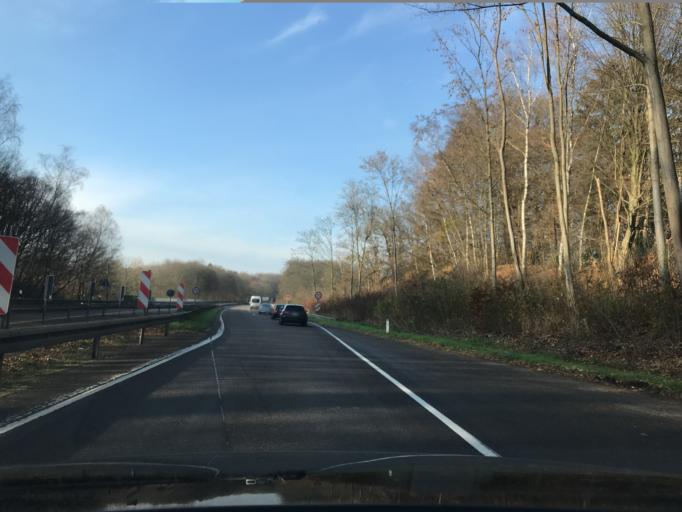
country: DE
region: North Rhine-Westphalia
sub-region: Regierungsbezirk Dusseldorf
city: Solingen
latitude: 51.1859
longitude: 7.1153
